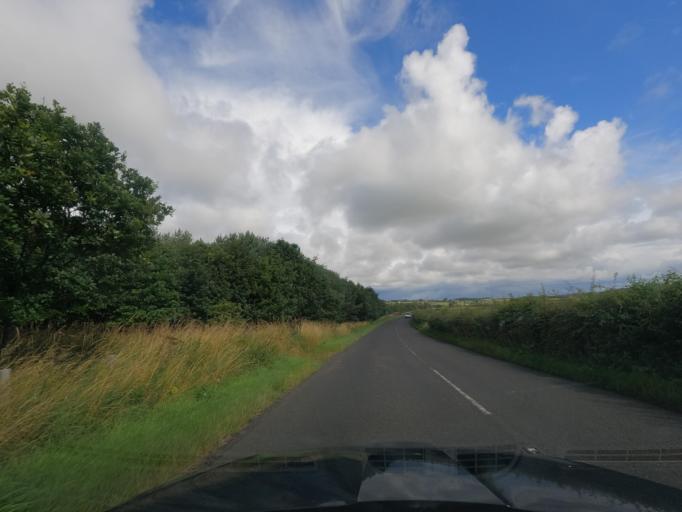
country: GB
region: England
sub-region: Northumberland
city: Lowick
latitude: 55.6132
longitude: -1.9988
